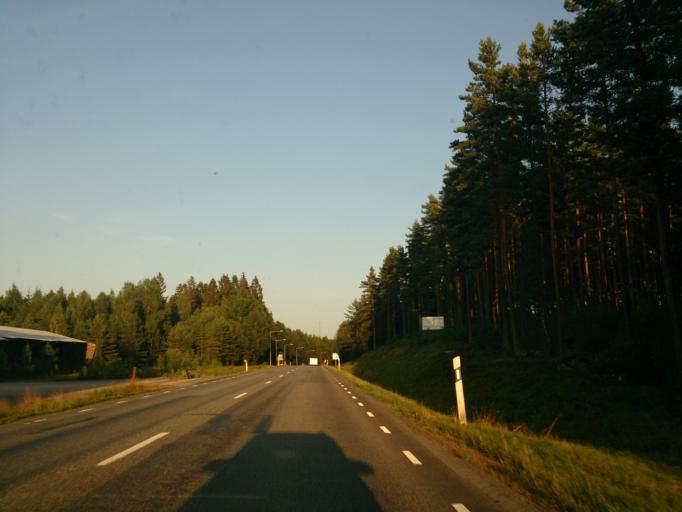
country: SE
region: Joenkoeping
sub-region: Varnamo Kommun
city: Bor
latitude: 57.1214
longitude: 14.1549
